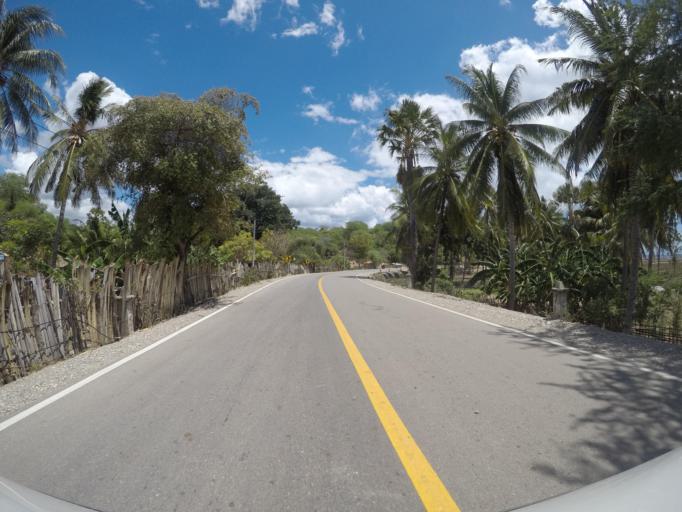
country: TL
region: Baucau
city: Baucau
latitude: -8.4089
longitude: 126.7298
